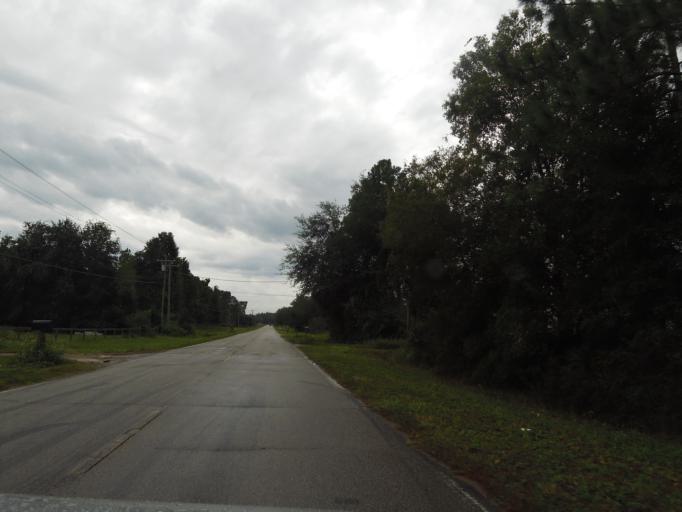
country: US
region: Florida
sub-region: Clay County
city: Middleburg
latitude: 30.1148
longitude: -81.9618
